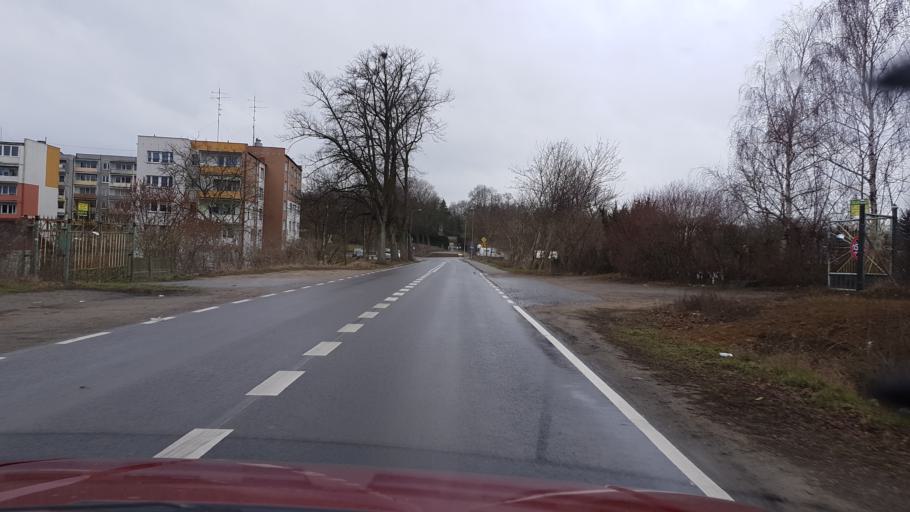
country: PL
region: West Pomeranian Voivodeship
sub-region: Powiat gryfinski
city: Gryfino
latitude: 53.2581
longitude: 14.5007
